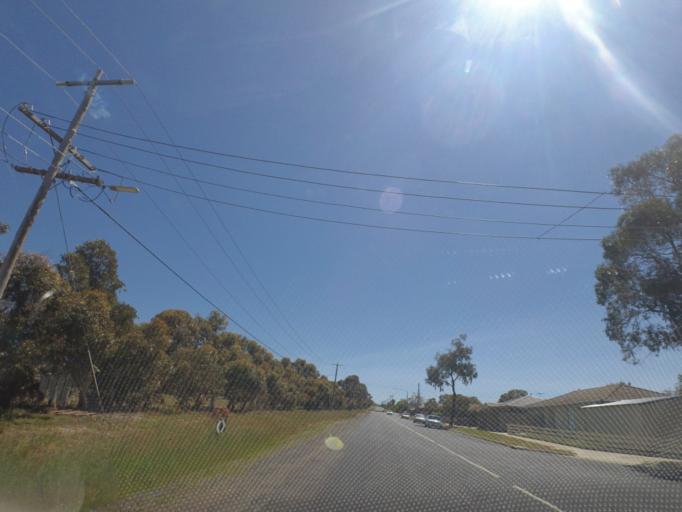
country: AU
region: Victoria
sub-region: Hume
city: Sunbury
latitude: -37.5782
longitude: 144.6935
